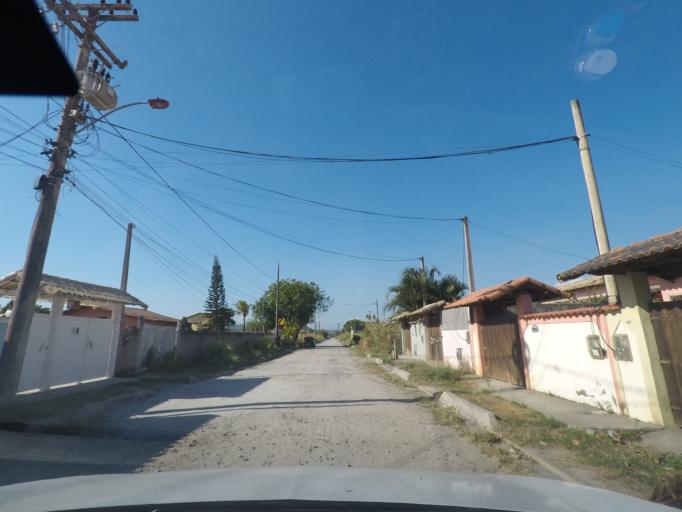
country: BR
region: Rio de Janeiro
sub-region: Marica
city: Marica
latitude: -22.9662
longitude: -42.9253
